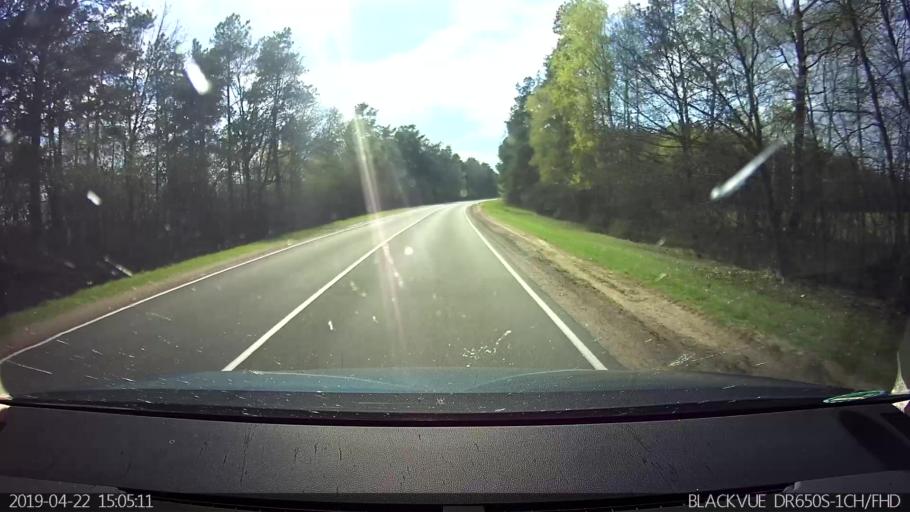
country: BY
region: Brest
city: Kamyanyets
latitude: 52.3353
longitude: 23.8740
